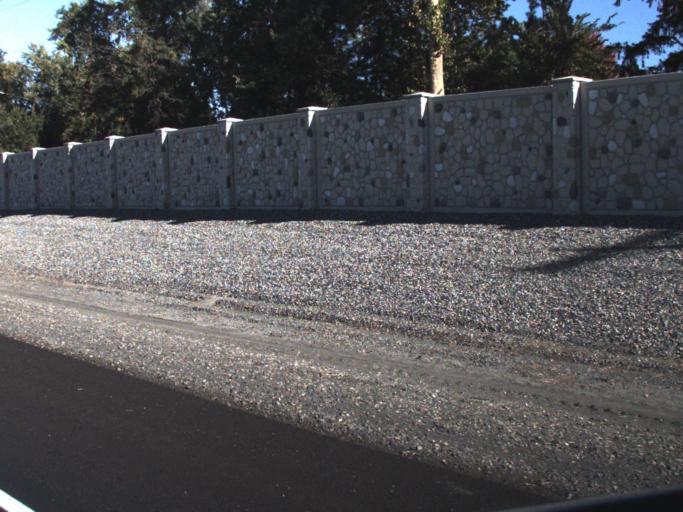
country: US
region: Washington
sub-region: Benton County
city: Richland
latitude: 46.2704
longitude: -119.3055
